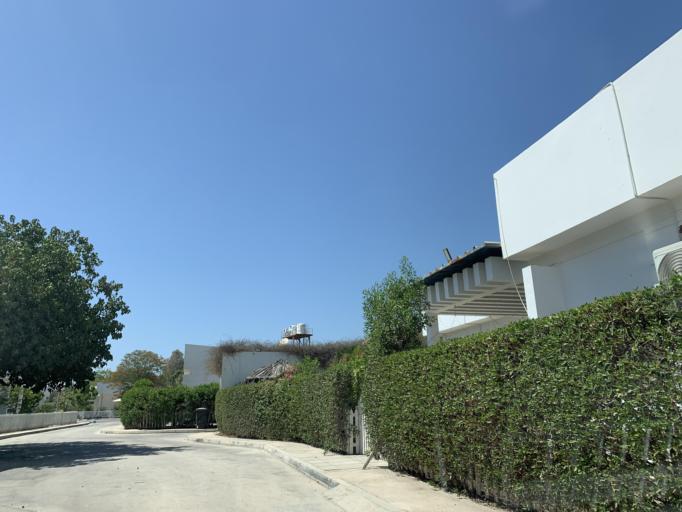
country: BH
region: Manama
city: Jidd Hafs
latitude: 26.2250
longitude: 50.4885
